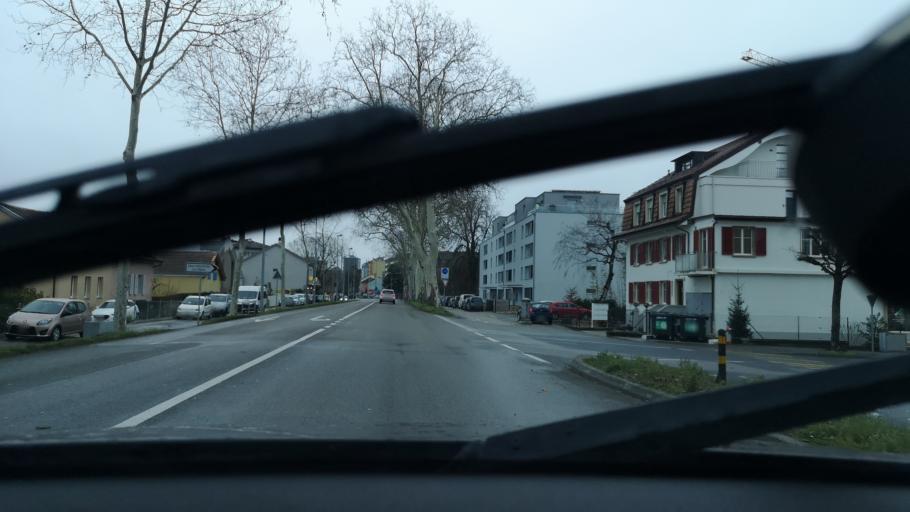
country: CH
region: Vaud
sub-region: Jura-Nord vaudois District
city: Yverdon-les-Bains
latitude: 46.7867
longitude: 6.6316
